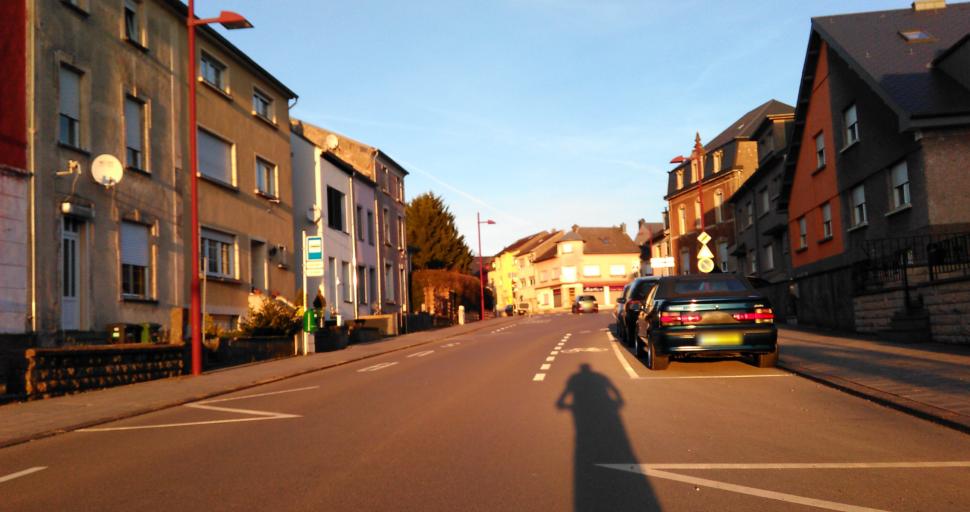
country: LU
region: Luxembourg
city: Lamadelaine
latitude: 49.5482
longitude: 5.8497
